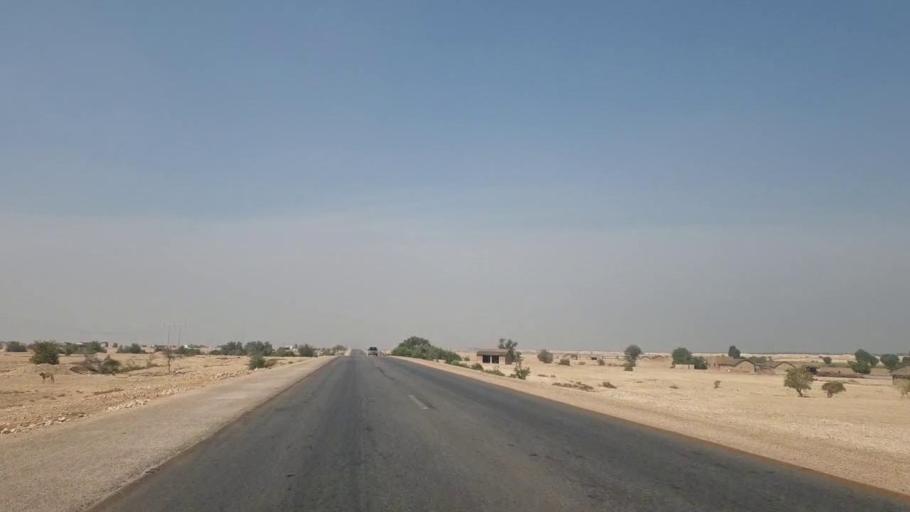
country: PK
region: Sindh
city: Hala
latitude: 25.8378
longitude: 68.2668
